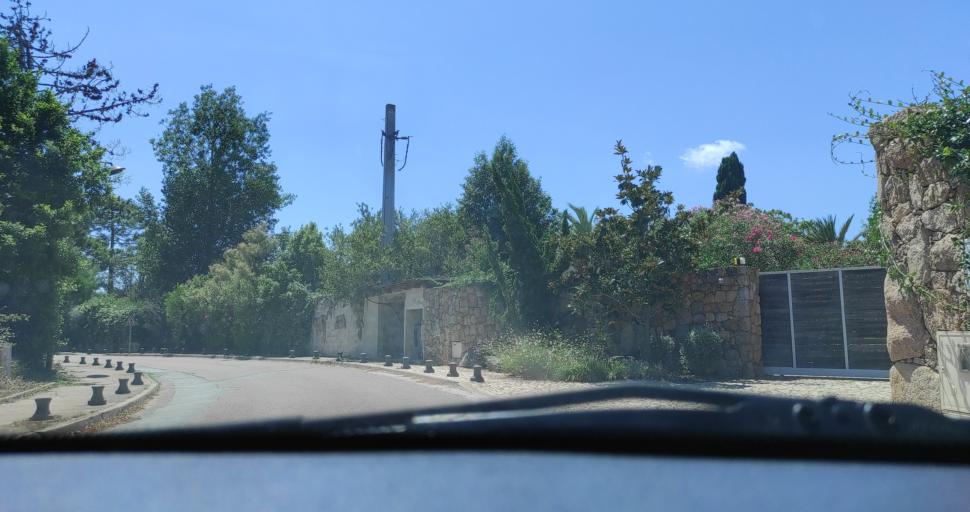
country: FR
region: Corsica
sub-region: Departement de la Corse-du-Sud
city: Porto-Vecchio
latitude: 41.6232
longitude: 9.3357
